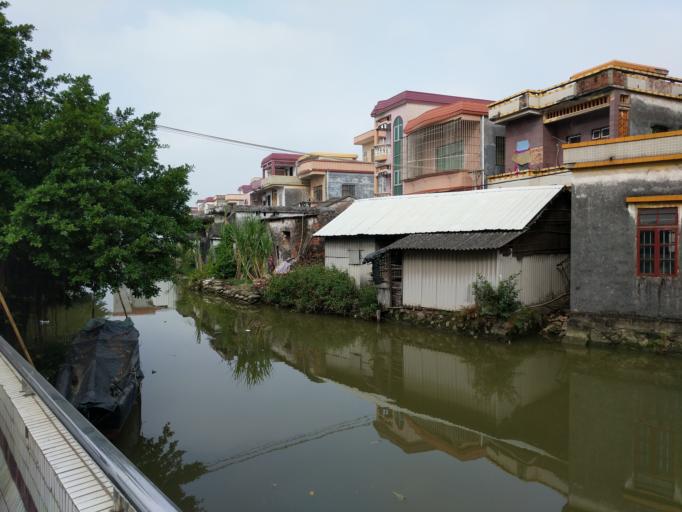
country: CN
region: Guangdong
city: Da'ao
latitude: 22.5210
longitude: 113.1785
